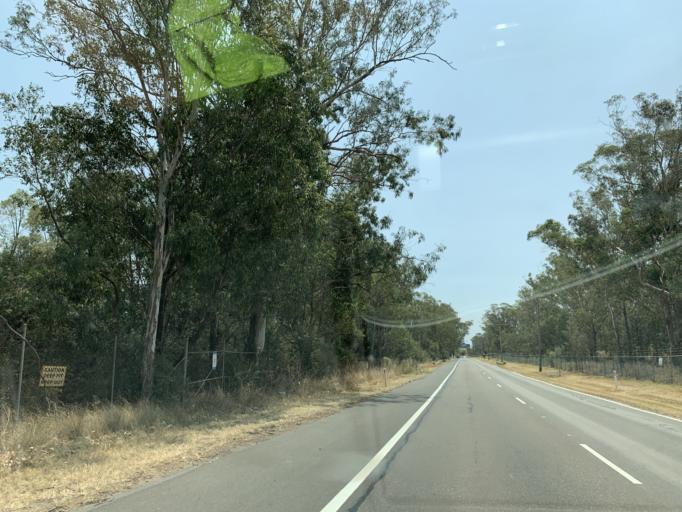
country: AU
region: New South Wales
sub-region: Fairfield
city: Horsley Park
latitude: -33.8274
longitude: 150.8721
